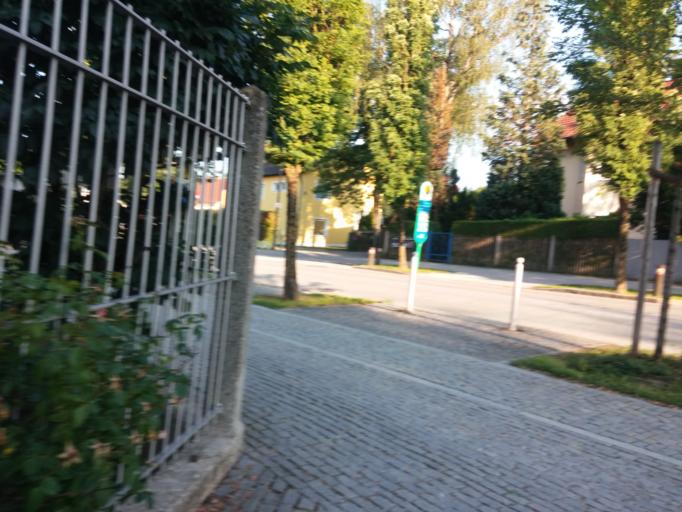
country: DE
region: Bavaria
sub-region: Upper Bavaria
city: Feldkirchen
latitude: 48.1476
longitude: 11.7355
